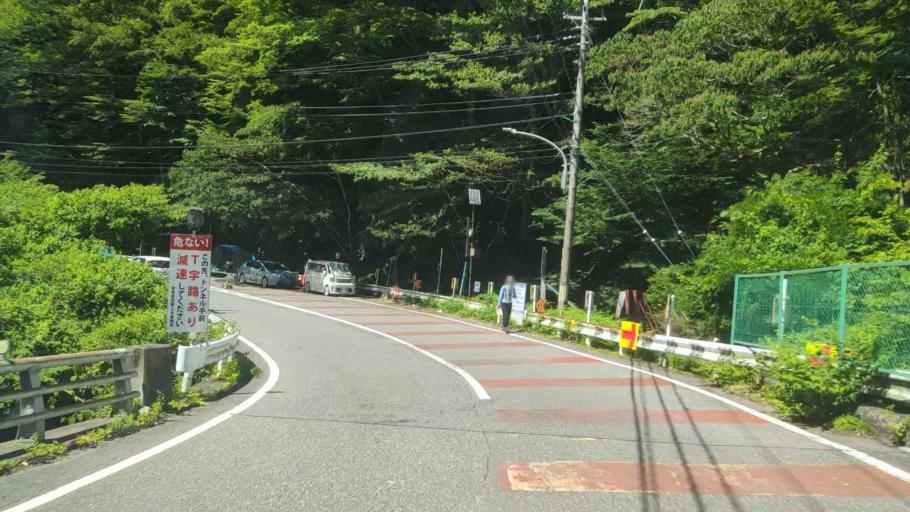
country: JP
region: Nara
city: Yoshino-cho
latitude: 34.2177
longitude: 135.9981
